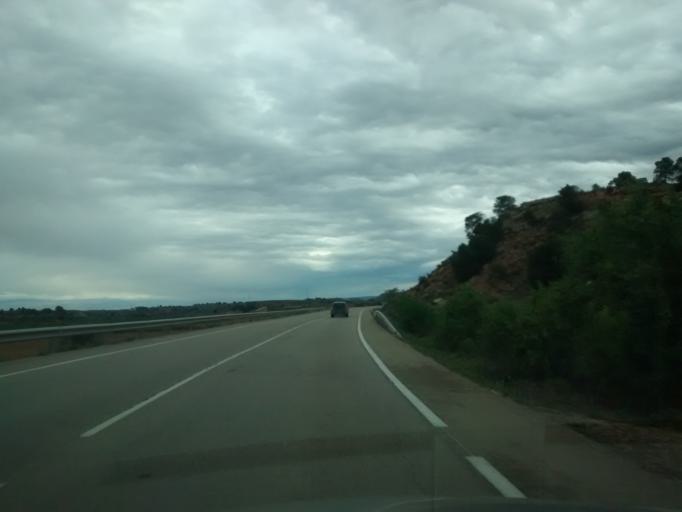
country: ES
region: Aragon
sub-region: Provincia de Zaragoza
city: Maella
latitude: 41.1796
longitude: 0.0514
